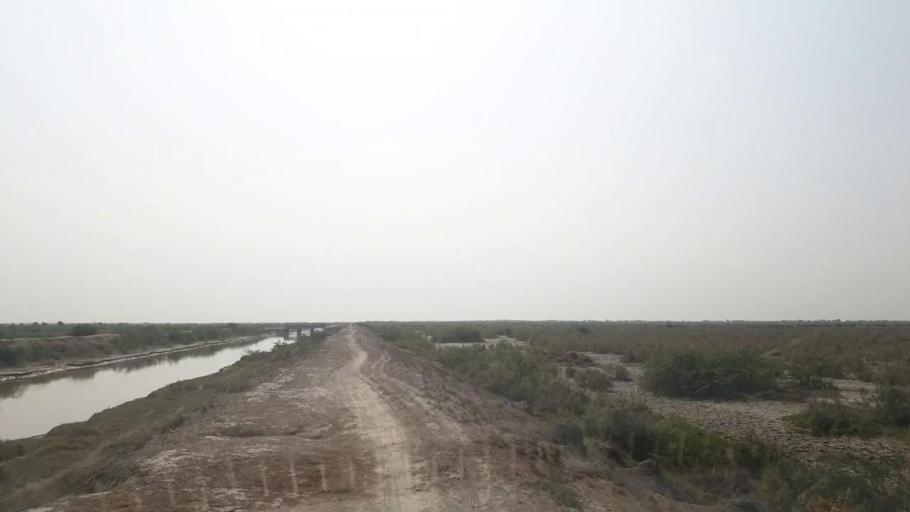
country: PK
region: Sindh
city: Kadhan
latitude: 24.3826
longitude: 68.8986
